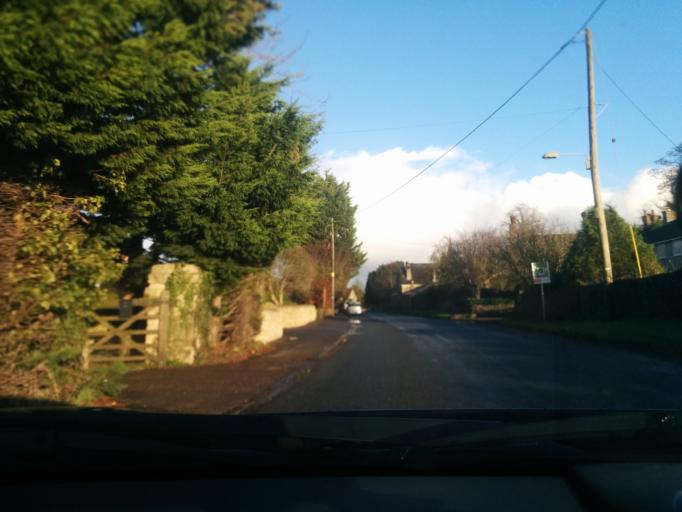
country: GB
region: England
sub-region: Oxfordshire
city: Abingdon
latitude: 51.6784
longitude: -1.3081
